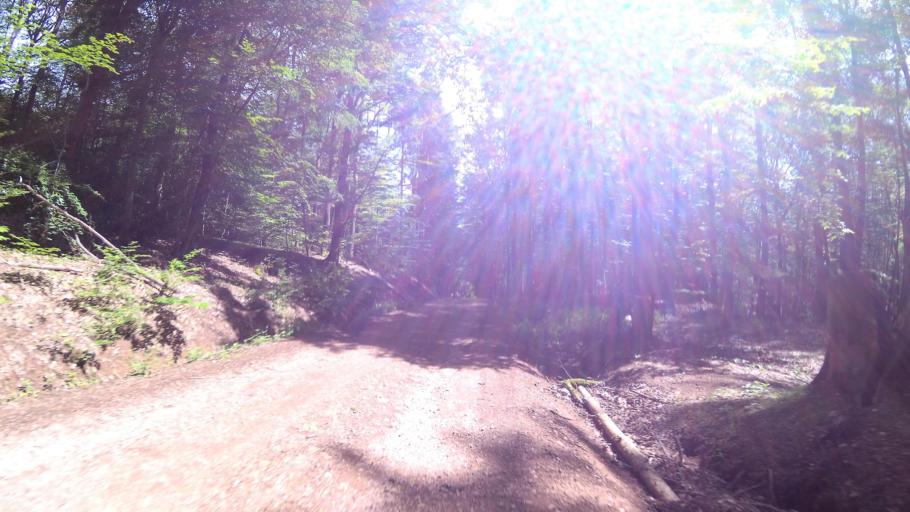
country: DE
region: Saarland
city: Oberthal
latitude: 49.5241
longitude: 7.0809
